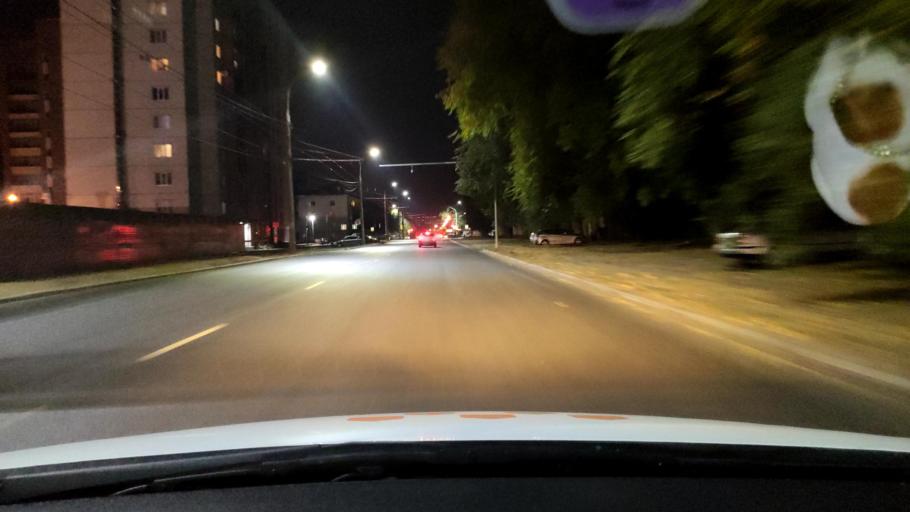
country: RU
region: Voronezj
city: Voronezh
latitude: 51.6983
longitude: 39.1858
